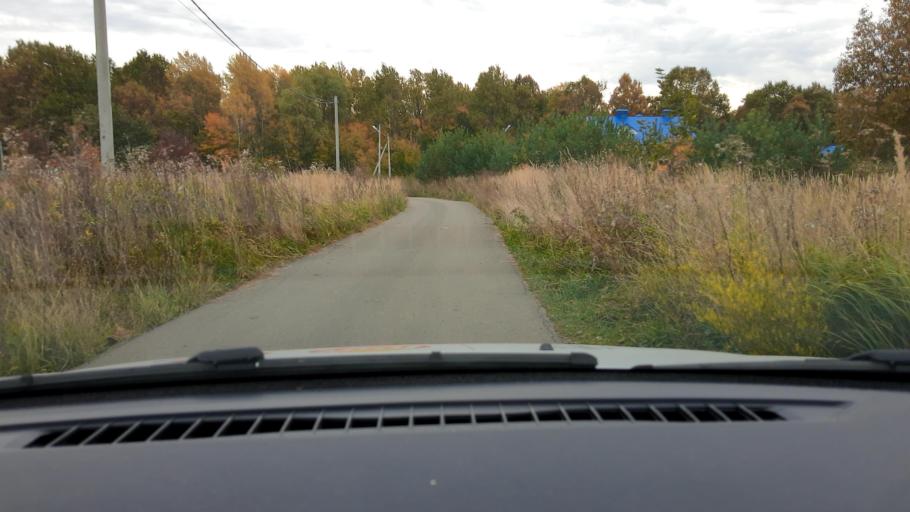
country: RU
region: Nizjnij Novgorod
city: Babino
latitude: 56.1284
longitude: 43.6482
